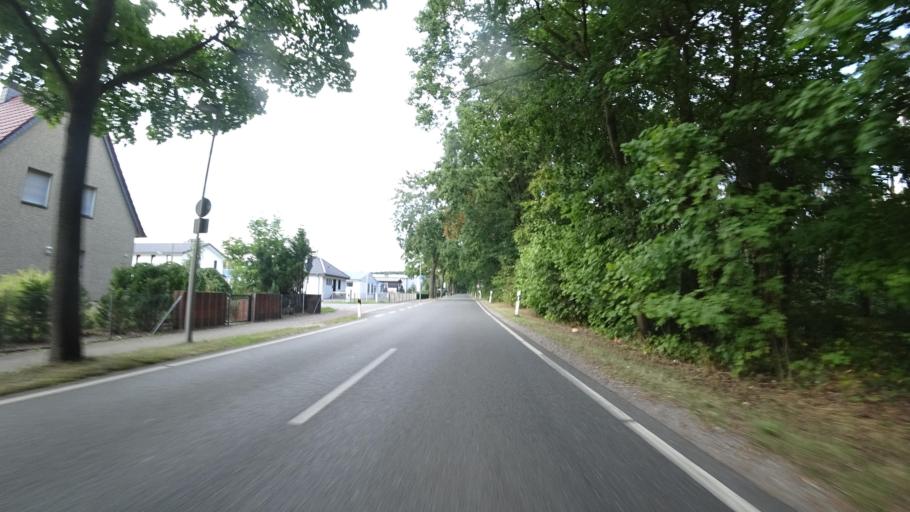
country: DE
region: North Rhine-Westphalia
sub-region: Regierungsbezirk Detmold
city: Steinhagen
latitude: 51.9841
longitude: 8.4628
